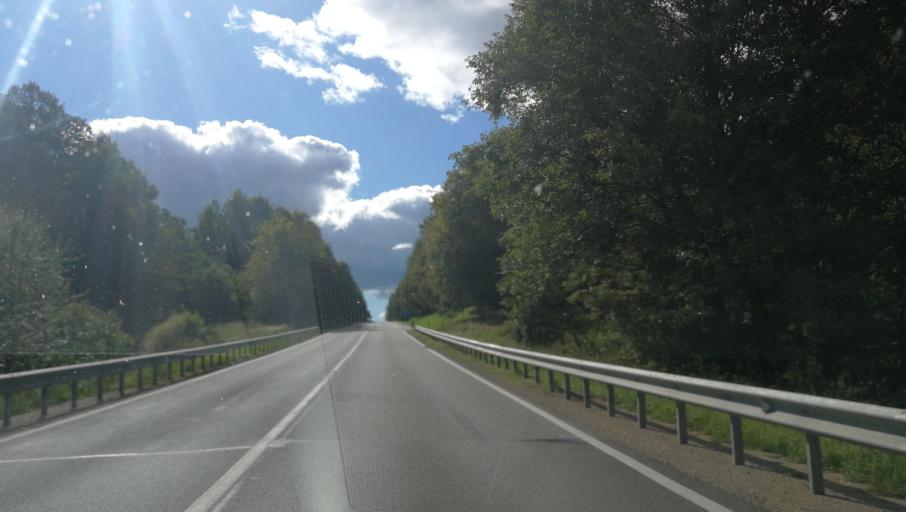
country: LV
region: Ligatne
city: Ligatne
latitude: 57.1872
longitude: 25.0578
